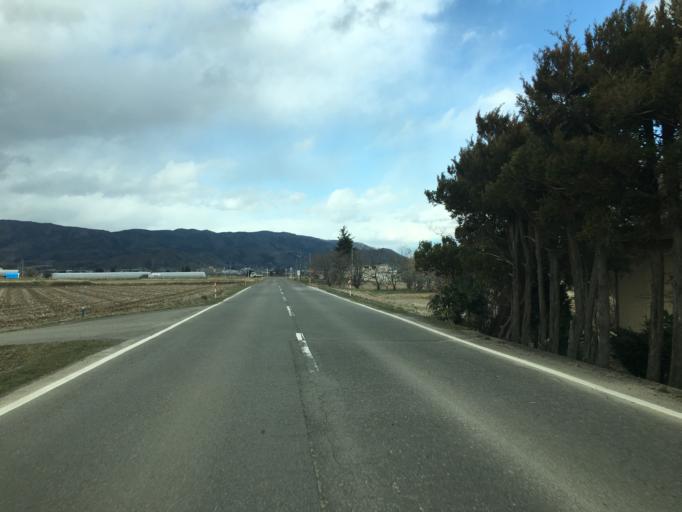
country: JP
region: Fukushima
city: Hobaramachi
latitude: 37.8533
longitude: 140.5339
